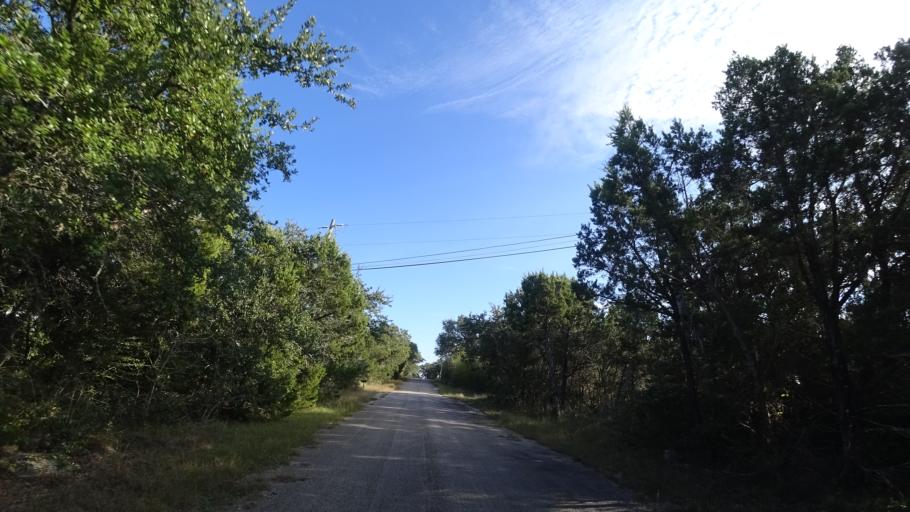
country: US
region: Texas
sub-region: Travis County
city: Barton Creek
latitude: 30.2459
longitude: -97.9193
